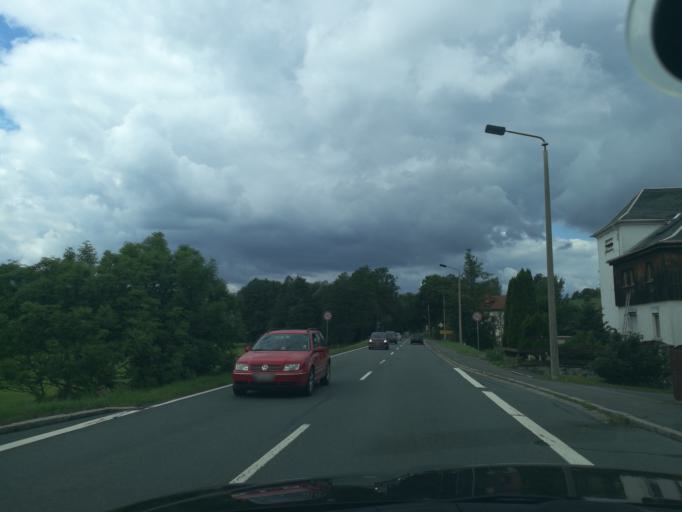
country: DE
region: Saxony
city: Eichigt
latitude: 50.3658
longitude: 12.2188
